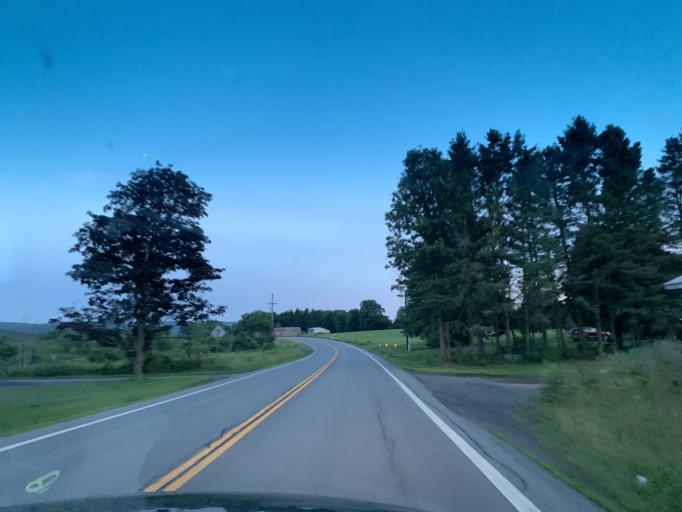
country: US
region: New York
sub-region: Chenango County
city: New Berlin
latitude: 42.6505
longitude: -75.3320
